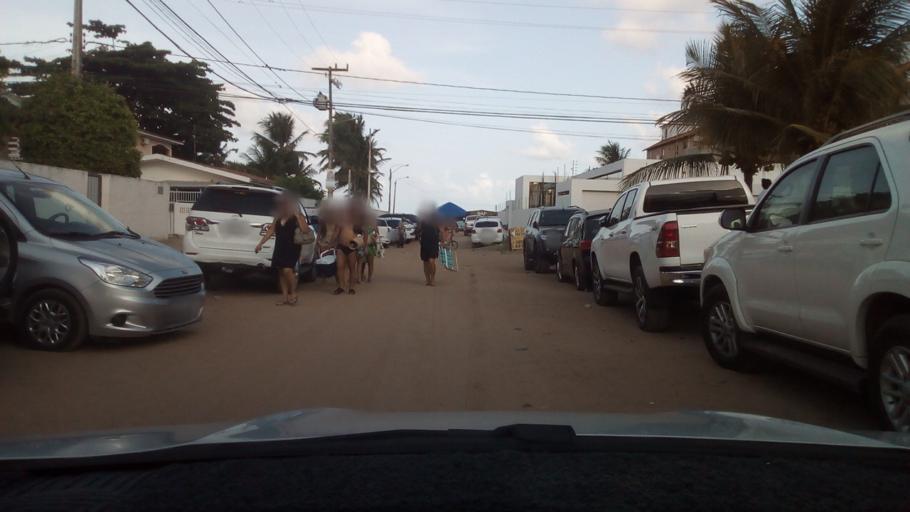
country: BR
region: Paraiba
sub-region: Cabedelo
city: Cabedelo
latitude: -7.0064
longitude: -34.8271
